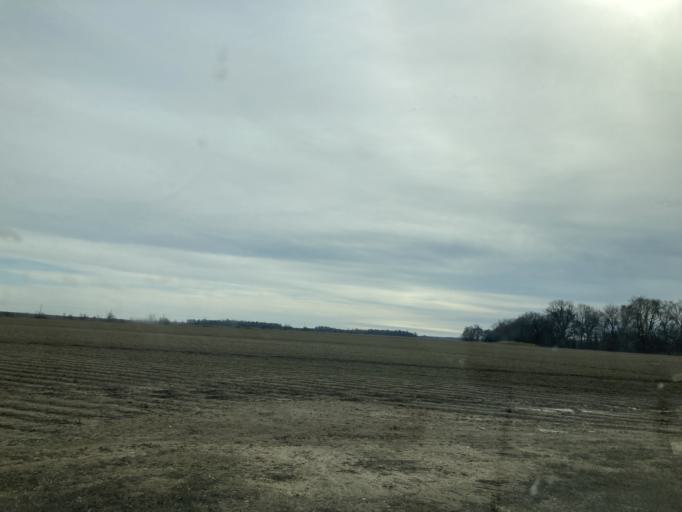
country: US
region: Mississippi
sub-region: Washington County
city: Hollandale
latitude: 33.1839
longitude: -90.6830
